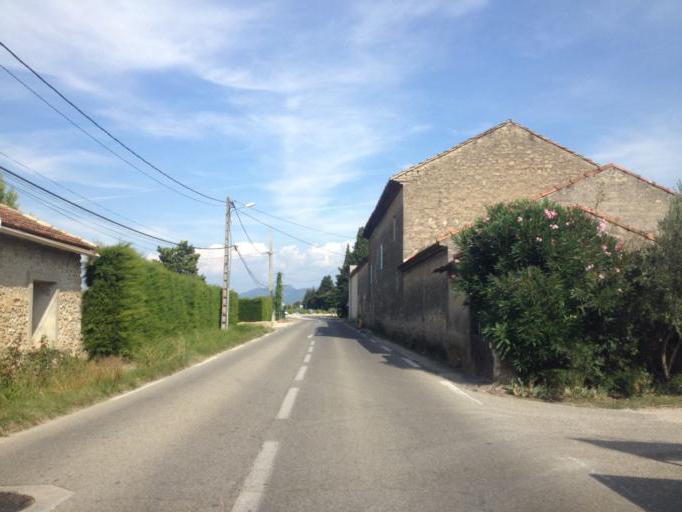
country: FR
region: Provence-Alpes-Cote d'Azur
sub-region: Departement du Vaucluse
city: Camaret-sur-Aigues
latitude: 44.1630
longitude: 4.8851
